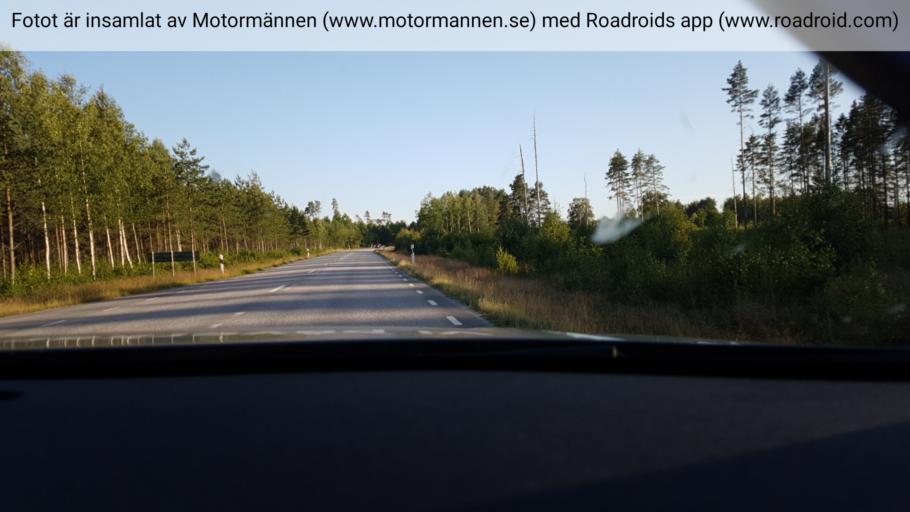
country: SE
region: Vaestra Goetaland
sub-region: Skovde Kommun
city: Stopen
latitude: 58.4409
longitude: 13.9357
